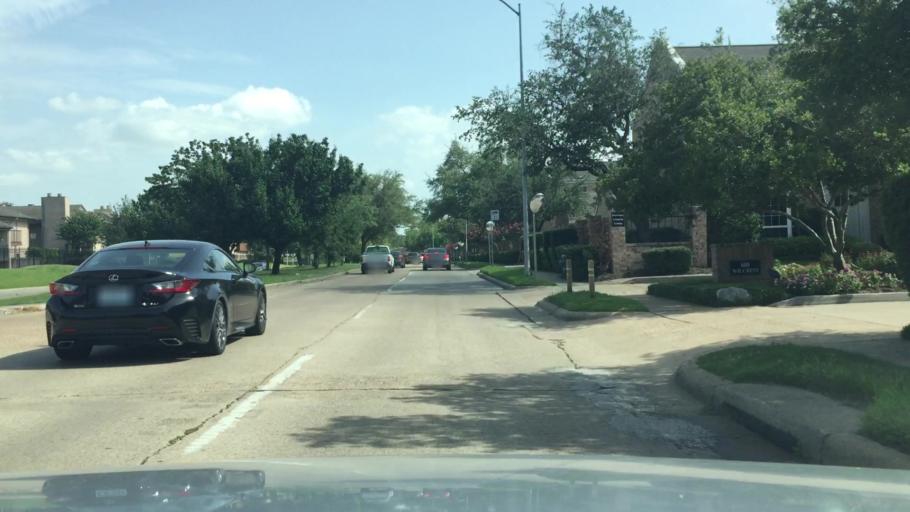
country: US
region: Texas
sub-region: Harris County
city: Bunker Hill Village
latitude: 29.7593
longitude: -95.5765
